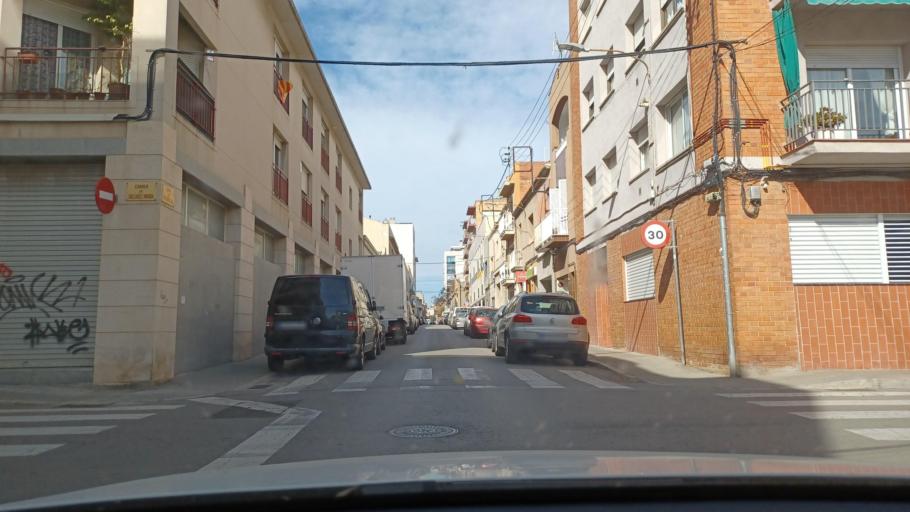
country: ES
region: Catalonia
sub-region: Provincia de Barcelona
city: Sabadell
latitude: 41.5380
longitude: 2.1144
